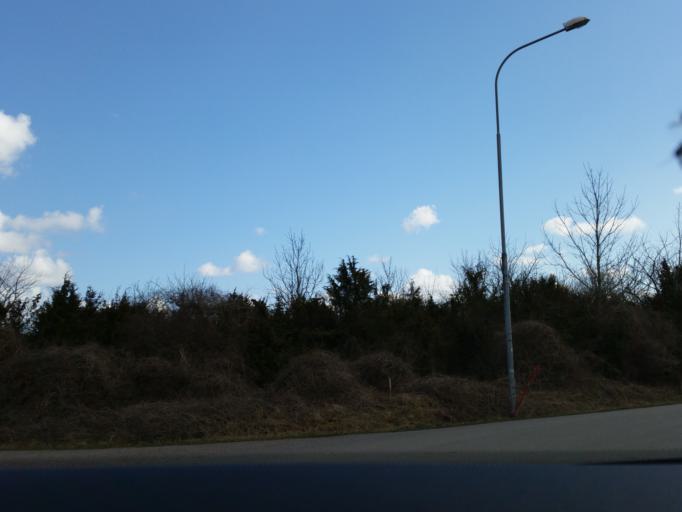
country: SE
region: Kalmar
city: Faerjestaden
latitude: 56.6827
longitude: 16.5310
